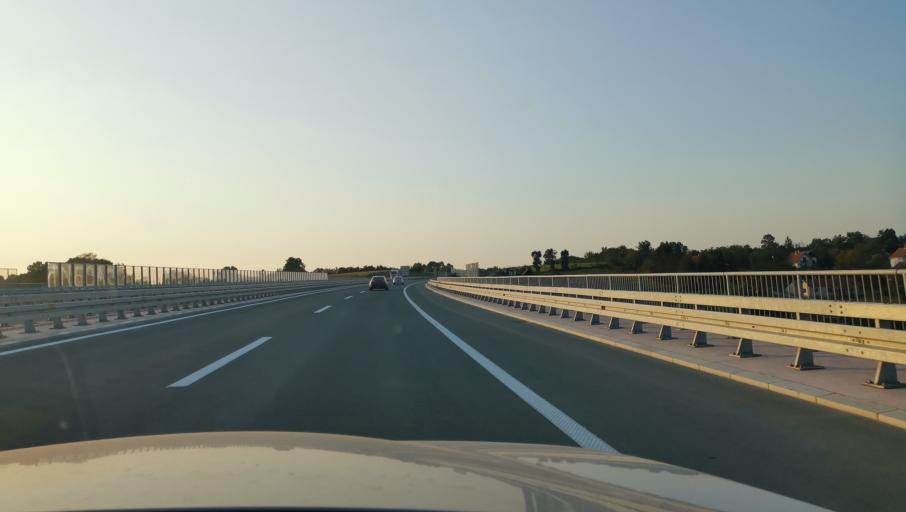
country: RS
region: Central Serbia
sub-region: Kolubarski Okrug
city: Lajkovac
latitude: 44.3622
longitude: 20.1224
